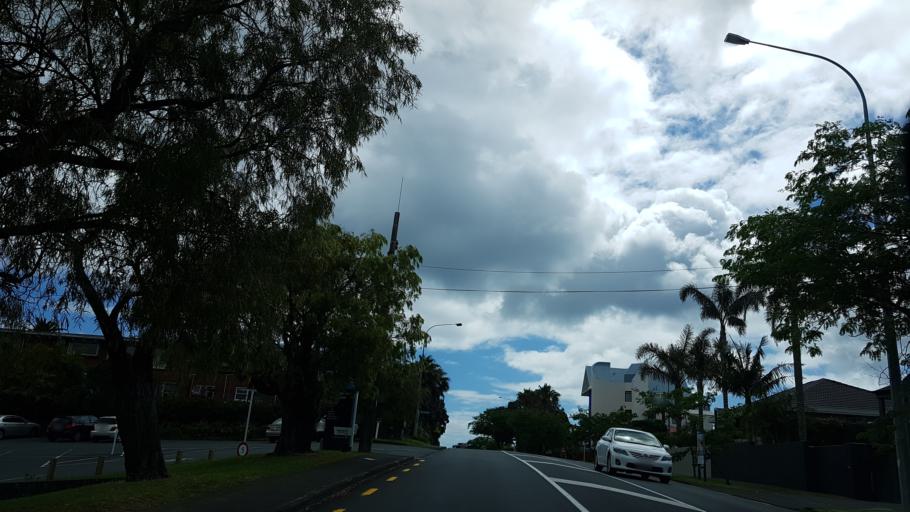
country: NZ
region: Auckland
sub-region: Auckland
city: North Shore
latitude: -36.7860
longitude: 174.7686
